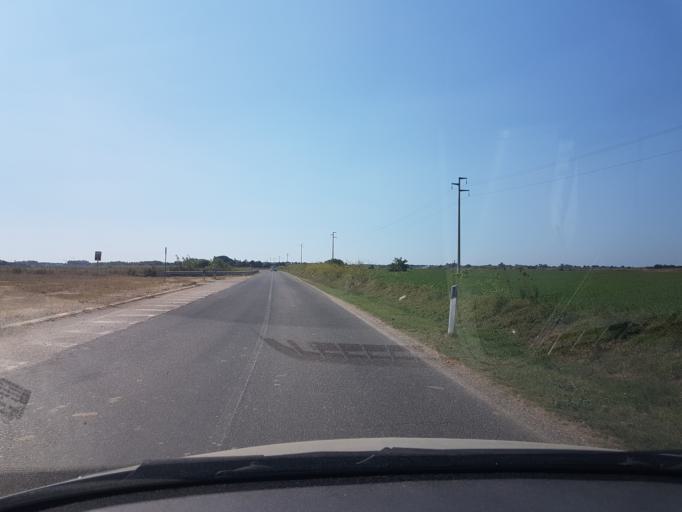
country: IT
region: Sardinia
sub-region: Provincia di Oristano
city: Riola Sardo
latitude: 40.0010
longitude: 8.5171
